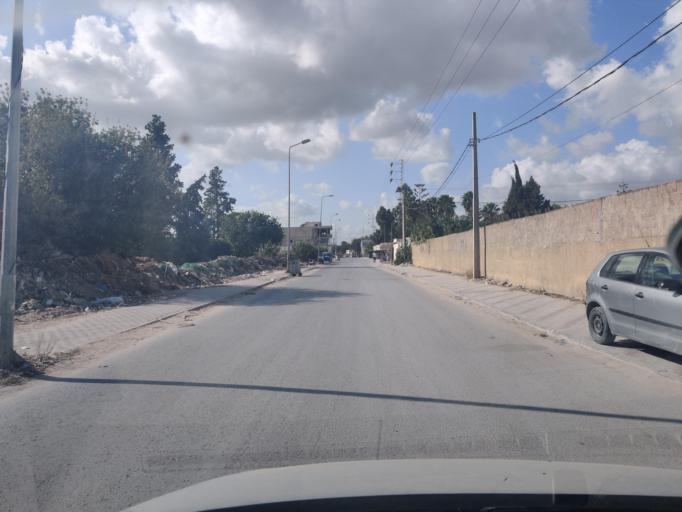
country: TN
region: Tunis
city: Al Marsa
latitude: 36.8792
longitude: 10.2728
